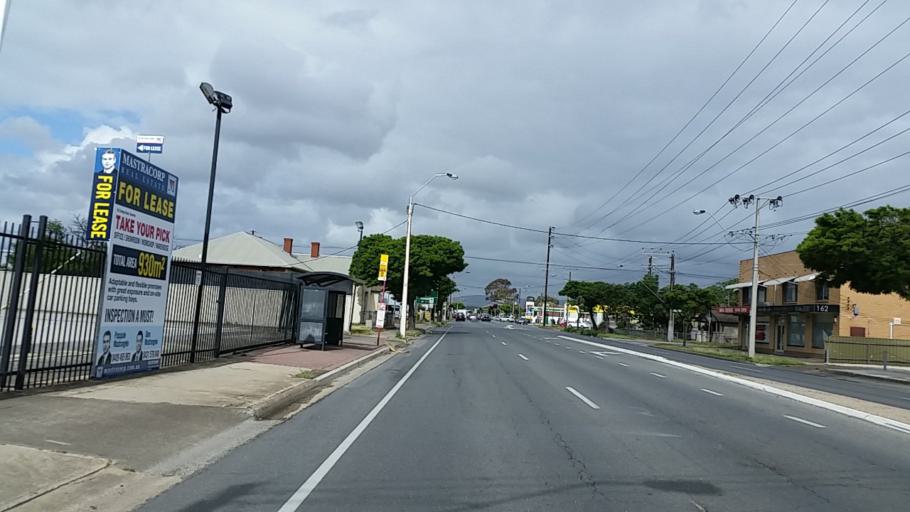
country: AU
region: South Australia
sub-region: Charles Sturt
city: Allenby Gardens
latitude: -34.9046
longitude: 138.5490
